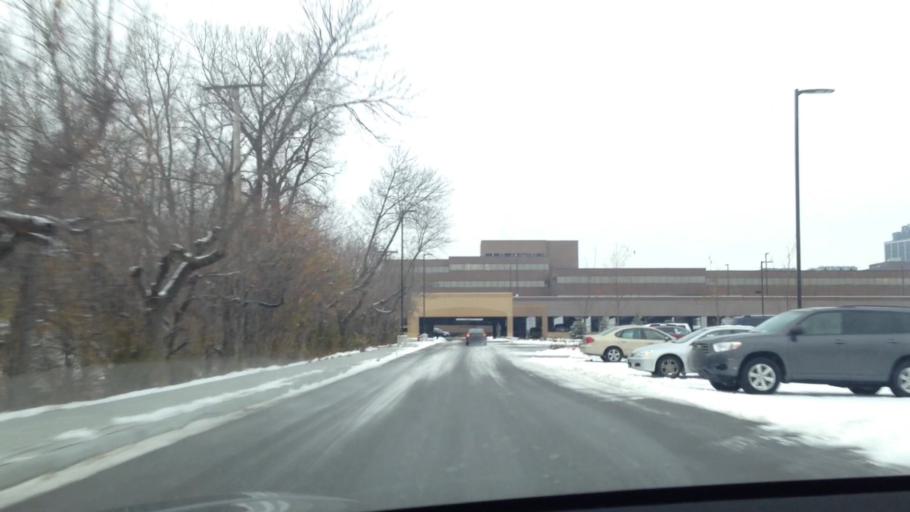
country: US
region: Minnesota
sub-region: Hennepin County
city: Edina
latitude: 44.8632
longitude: -93.3336
